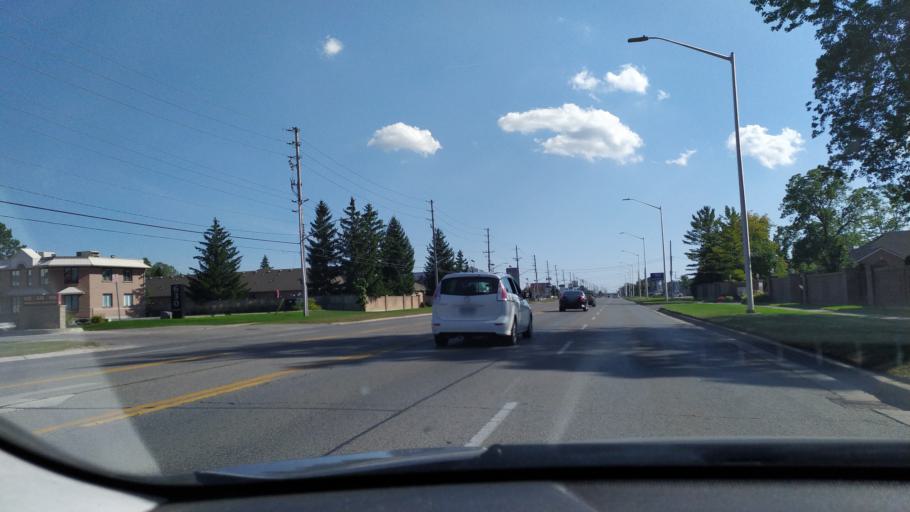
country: CA
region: Ontario
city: London
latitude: 42.9522
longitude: -81.2595
